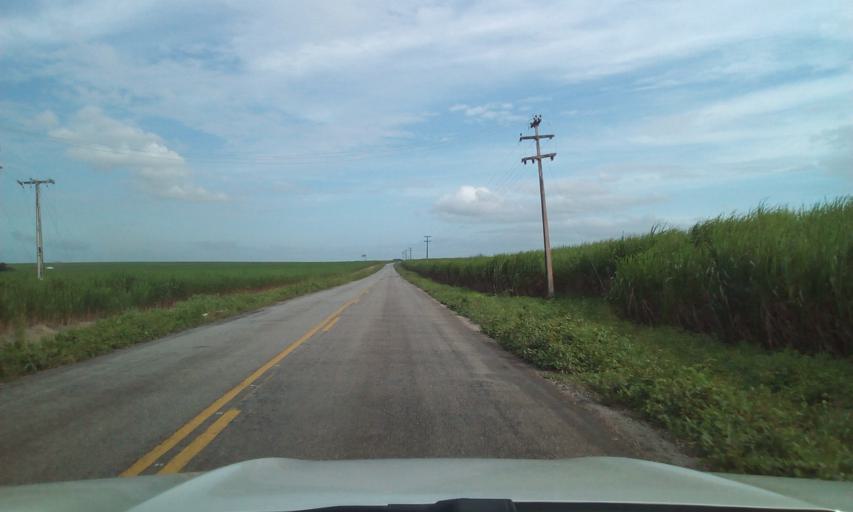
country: BR
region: Paraiba
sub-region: Santa Rita
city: Santa Rita
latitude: -7.0116
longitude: -34.9842
